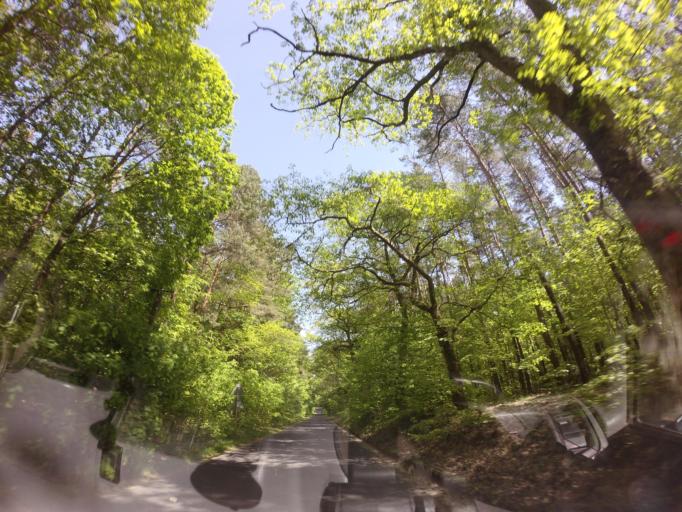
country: PL
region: West Pomeranian Voivodeship
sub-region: Powiat mysliborski
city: Barlinek
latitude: 52.9275
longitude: 15.1563
